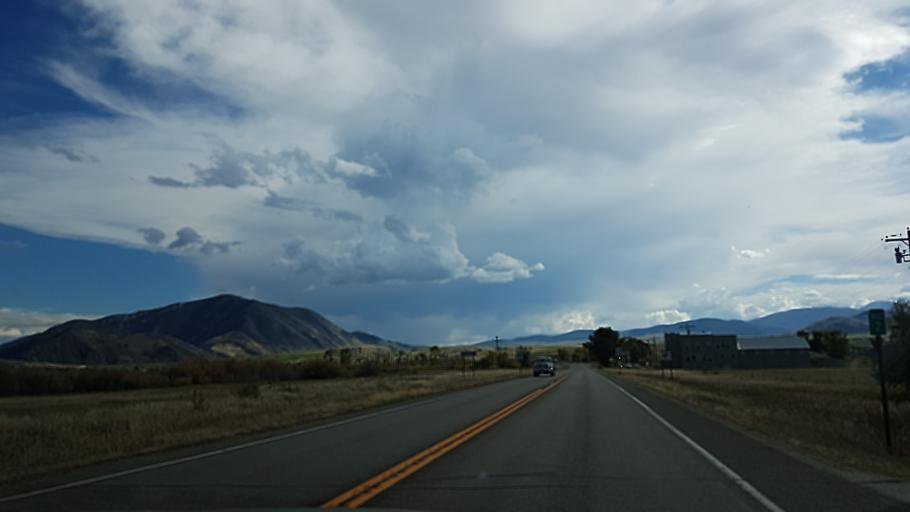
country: US
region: Montana
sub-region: Jefferson County
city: Whitehall
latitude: 45.8592
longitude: -111.9523
